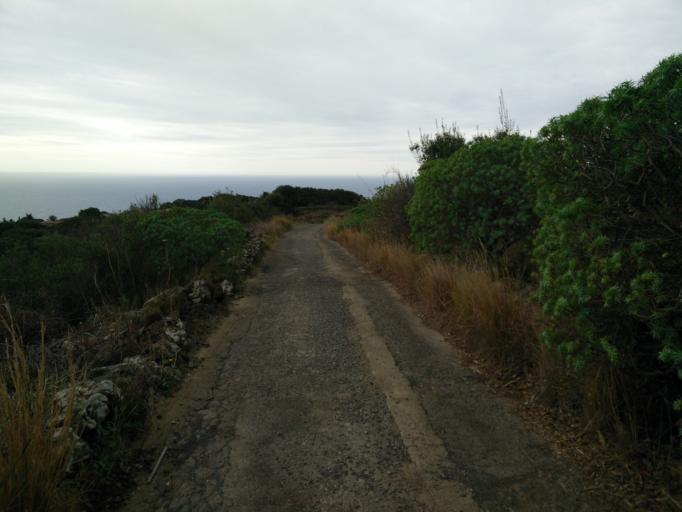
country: IT
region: Sicily
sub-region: Trapani
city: Kamma
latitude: 36.7505
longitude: 11.9973
